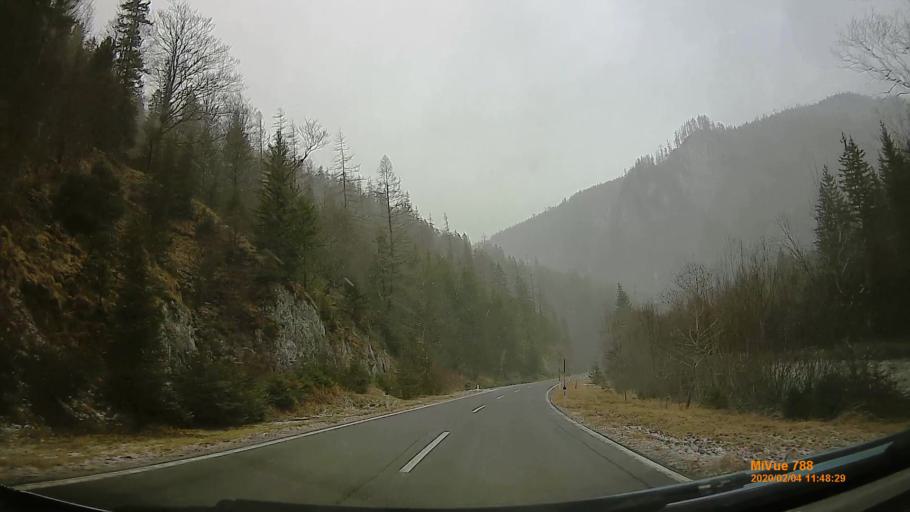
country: AT
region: Styria
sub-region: Politischer Bezirk Bruck-Muerzzuschlag
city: Muerzsteg
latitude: 47.7196
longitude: 15.4783
